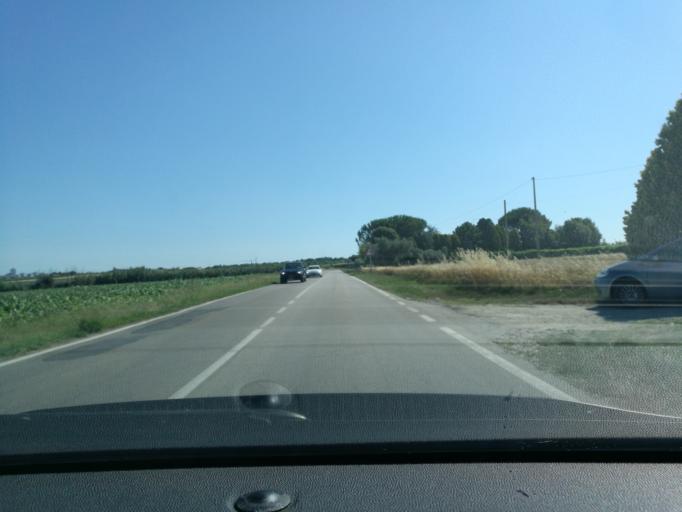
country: IT
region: Abruzzo
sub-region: Provincia di Chieti
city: Vasto
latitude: 42.1596
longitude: 14.7028
